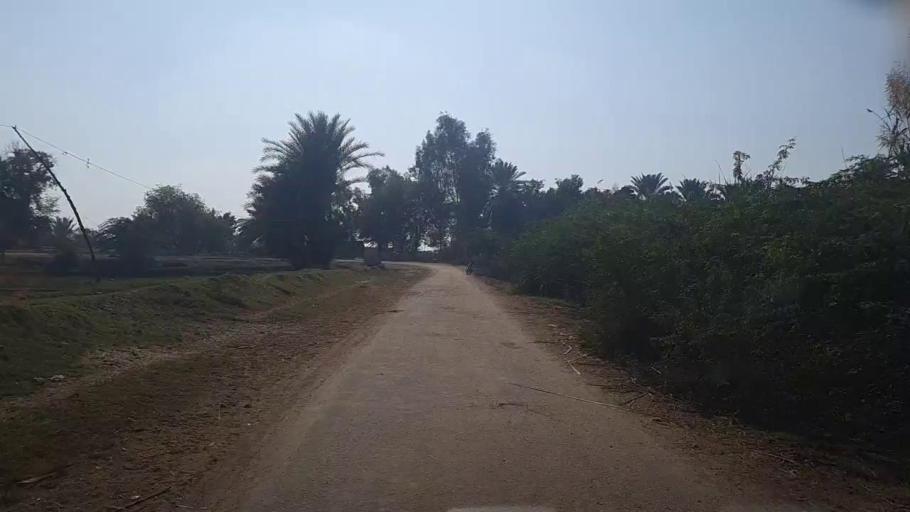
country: PK
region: Sindh
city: Kot Diji
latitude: 27.4227
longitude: 68.7372
